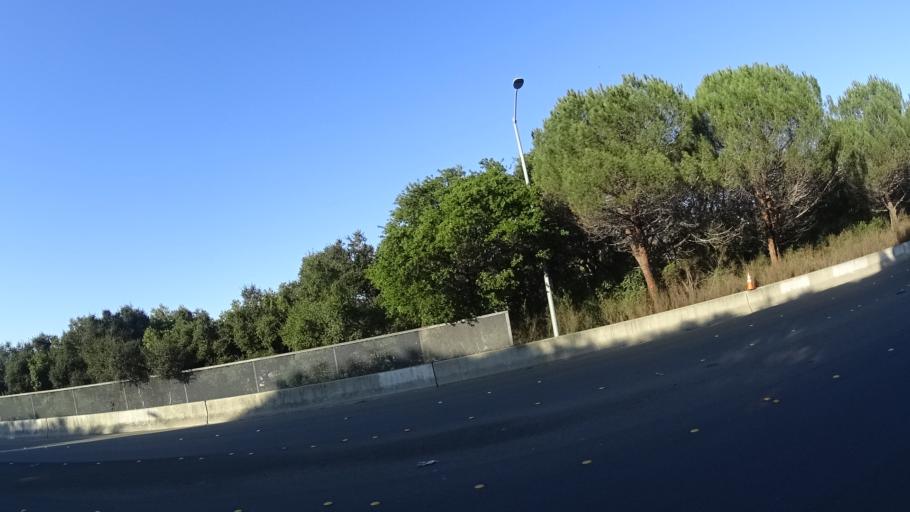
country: US
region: California
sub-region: Alameda County
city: Hayward
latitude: 37.6598
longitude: -122.0604
